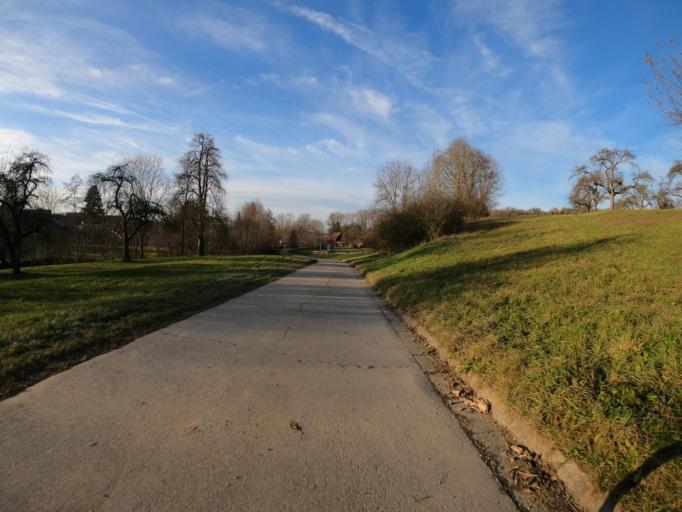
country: DE
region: Baden-Wuerttemberg
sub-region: Regierungsbezirk Stuttgart
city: Zell unter Aichelberg
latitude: 48.6533
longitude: 9.5882
